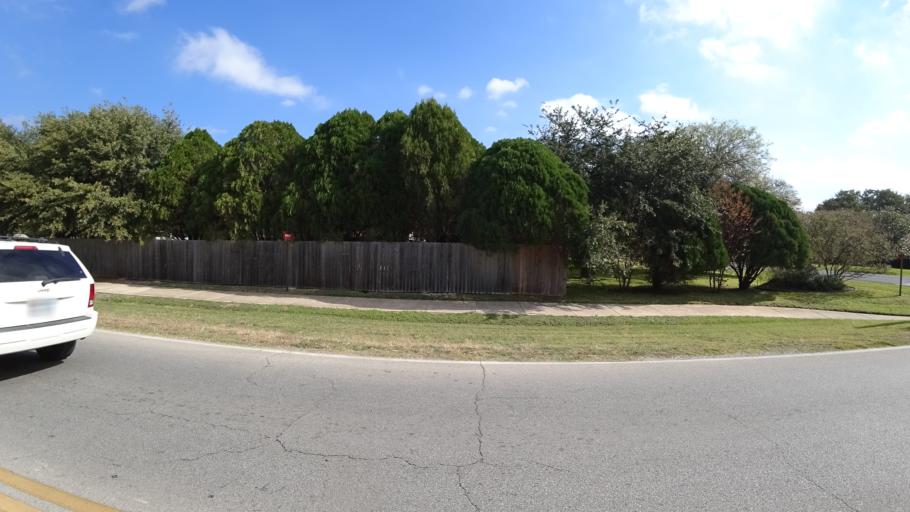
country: US
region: Texas
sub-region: Travis County
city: Shady Hollow
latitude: 30.1618
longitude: -97.8601
